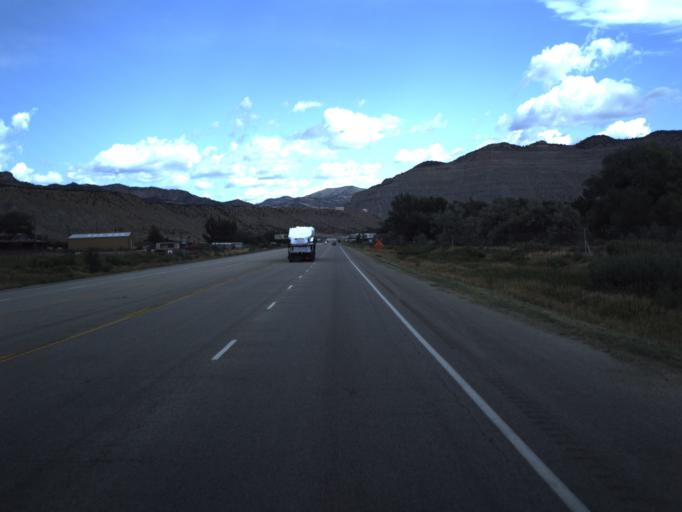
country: US
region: Utah
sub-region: Carbon County
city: Spring Glen
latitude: 39.6573
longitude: -110.8605
